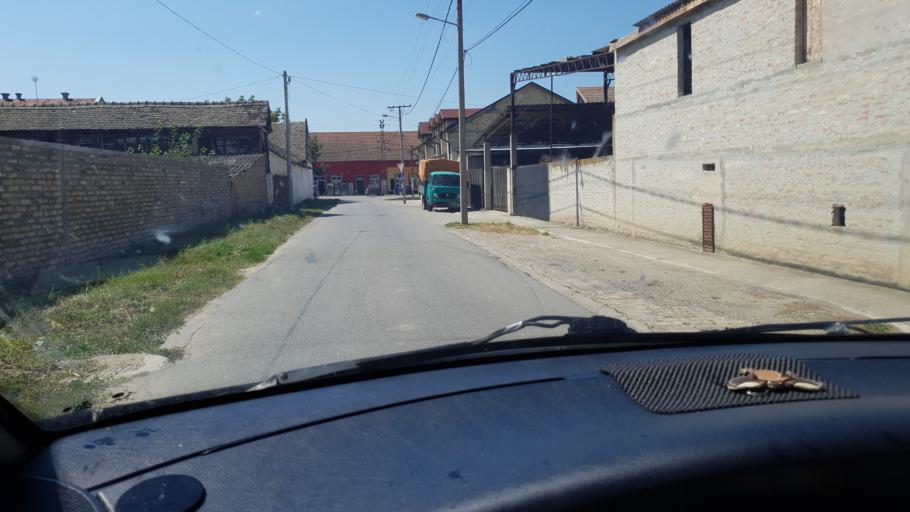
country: RS
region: Autonomna Pokrajina Vojvodina
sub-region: Juznobacki Okrug
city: Kovilj
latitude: 45.2260
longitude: 20.0224
